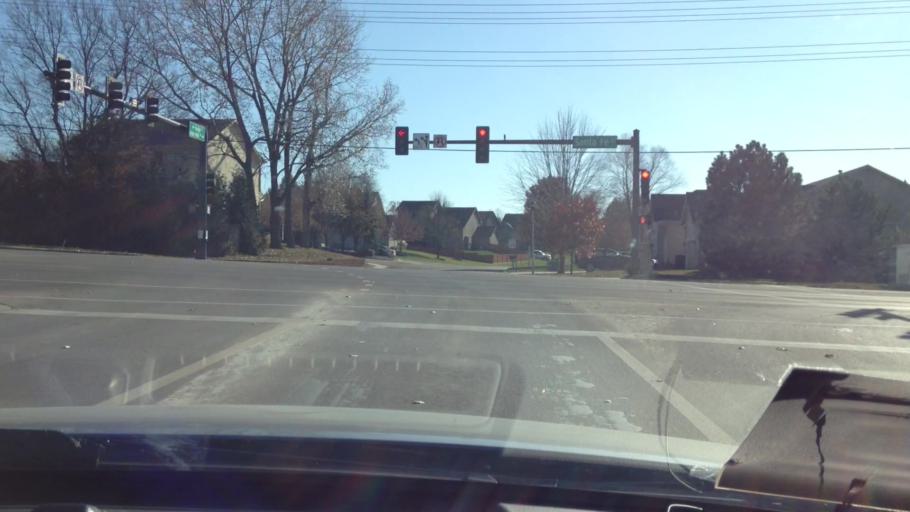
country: US
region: Kansas
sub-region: Johnson County
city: Olathe
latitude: 38.8840
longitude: -94.8498
